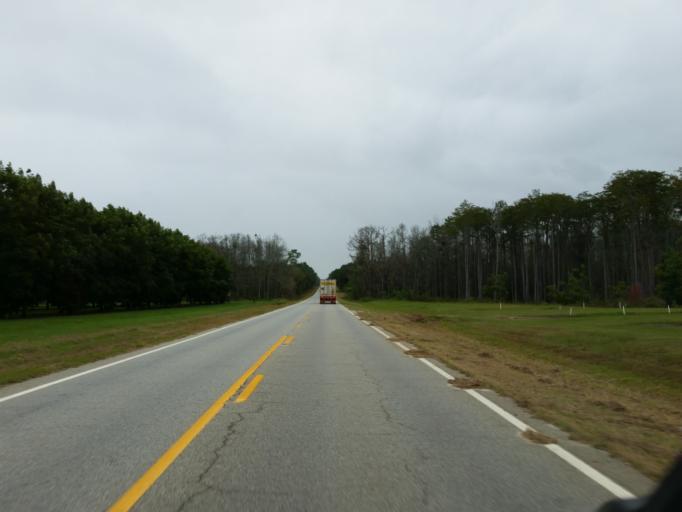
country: US
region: Georgia
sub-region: Berrien County
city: Ray City
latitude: 31.0891
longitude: -83.2460
